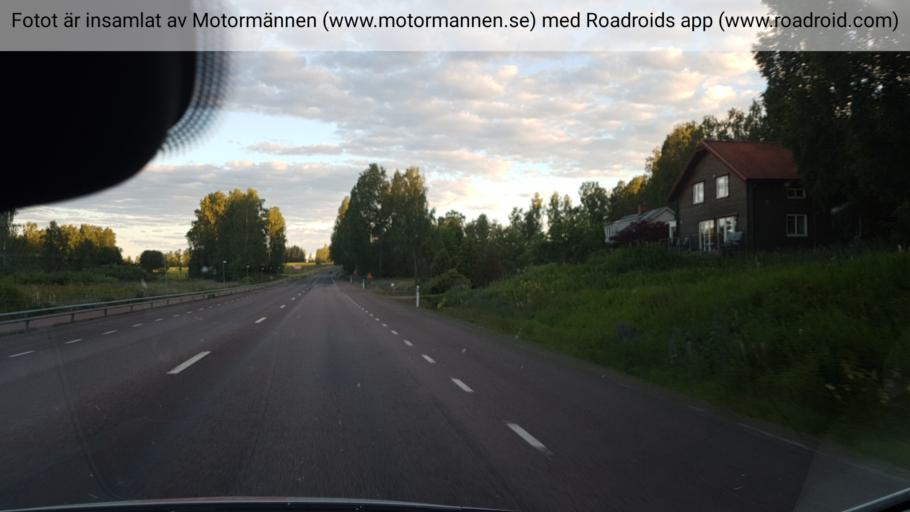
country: SE
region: Vaermland
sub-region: Sunne Kommun
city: Sunne
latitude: 59.8200
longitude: 13.1309
